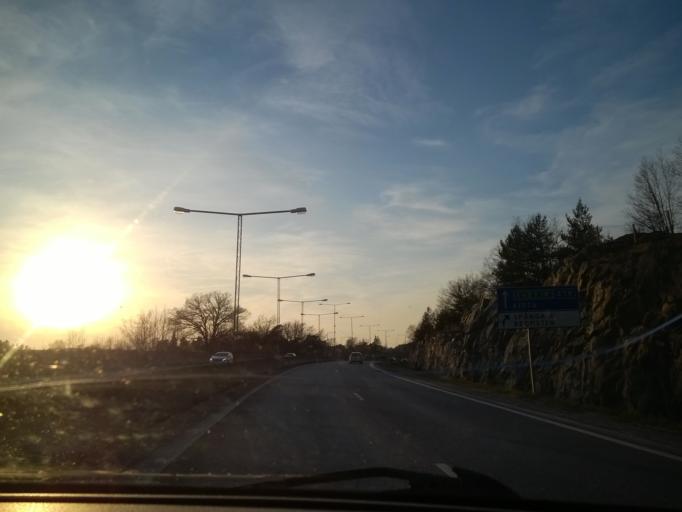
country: SE
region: Stockholm
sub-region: Stockholms Kommun
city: Kista
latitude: 59.3728
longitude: 17.9307
